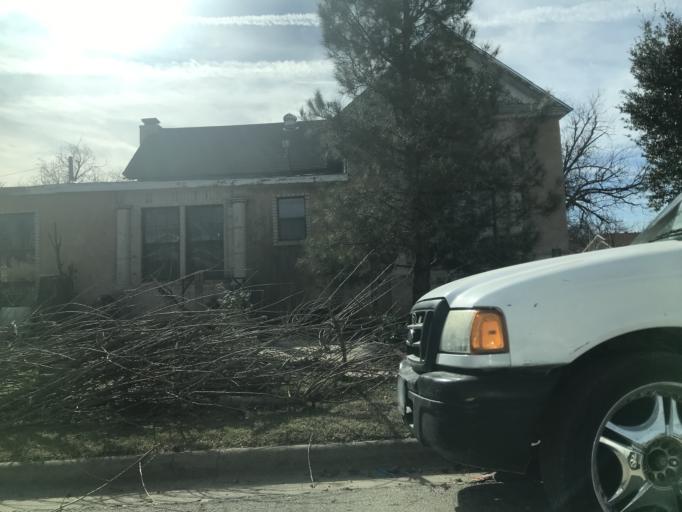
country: US
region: Texas
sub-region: Taylor County
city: Abilene
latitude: 32.4439
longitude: -99.7422
